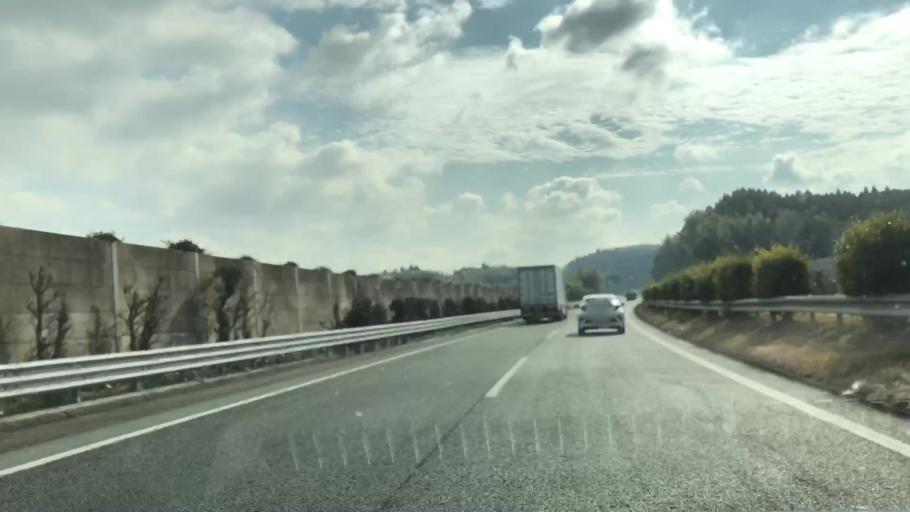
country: JP
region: Fukuoka
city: Setakamachi-takayanagi
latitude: 33.0840
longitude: 130.5417
